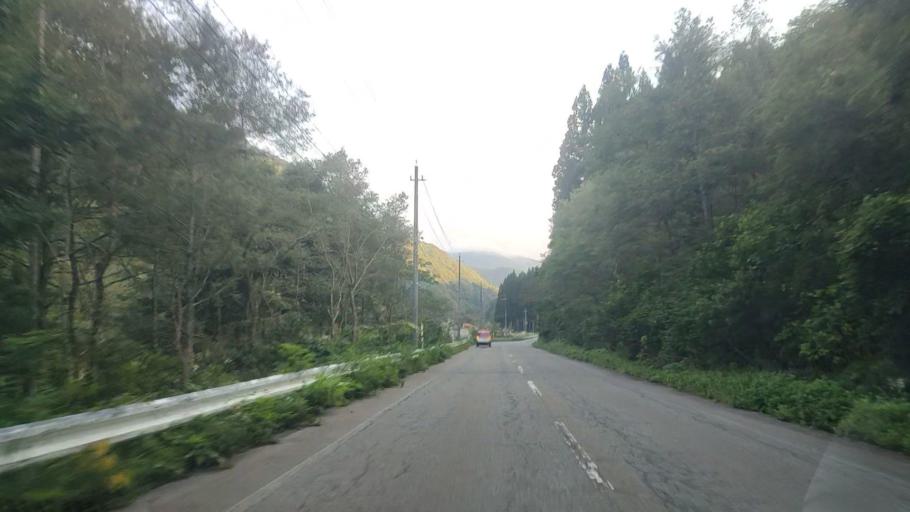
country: JP
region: Toyama
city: Yatsuomachi-higashikumisaka
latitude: 36.4822
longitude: 137.0481
